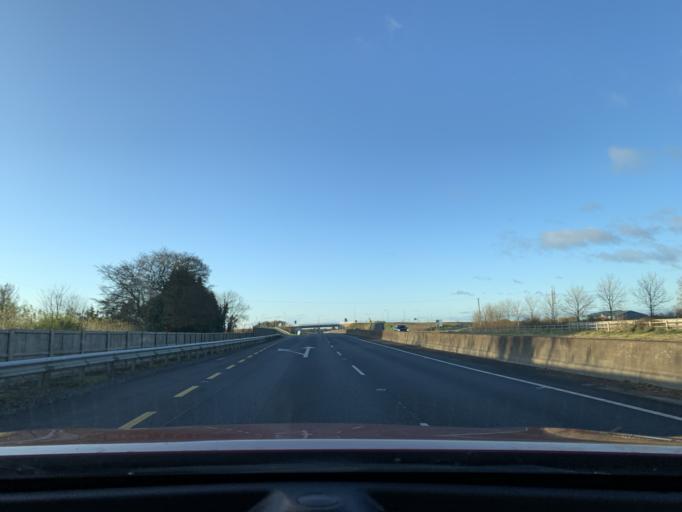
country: IE
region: Leinster
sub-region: An Iarmhi
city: Rathwire
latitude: 53.4986
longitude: -7.2300
